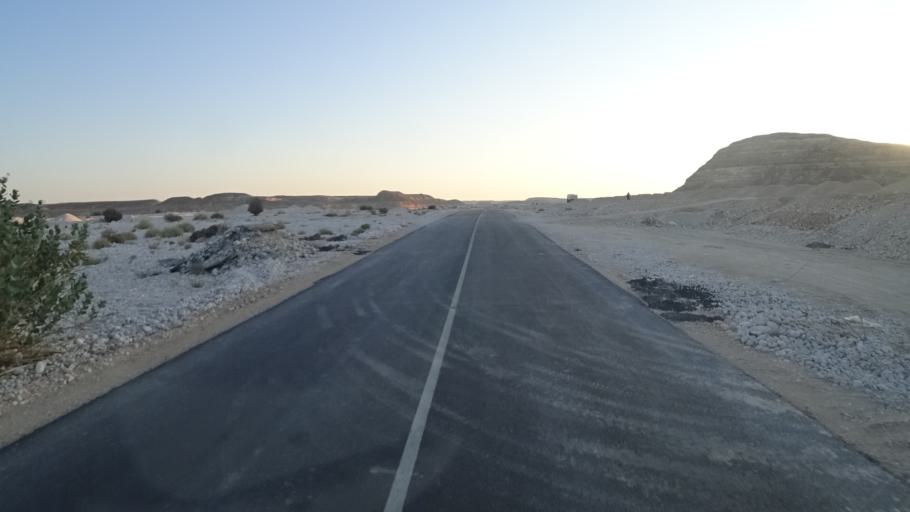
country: OM
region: Zufar
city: Salalah
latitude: 17.5202
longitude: 53.3765
